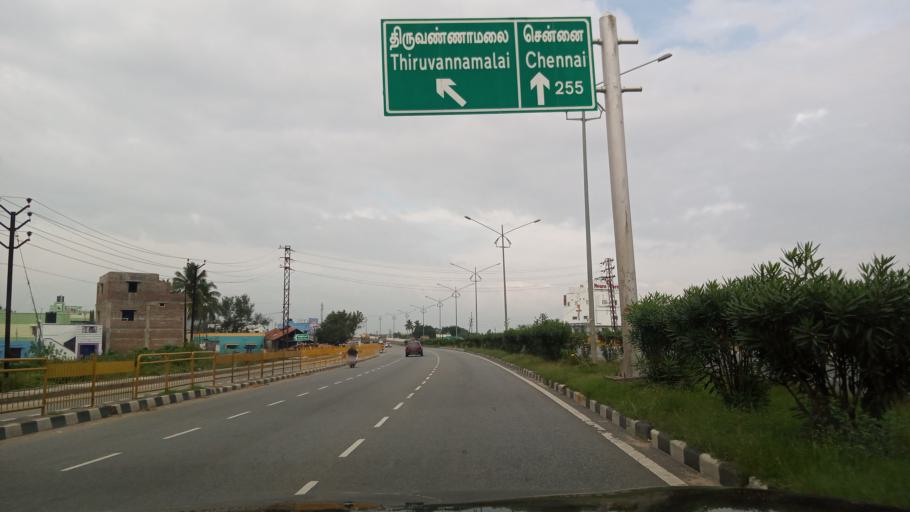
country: IN
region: Tamil Nadu
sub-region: Krishnagiri
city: Krishnagiri
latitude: 12.5105
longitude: 78.2277
